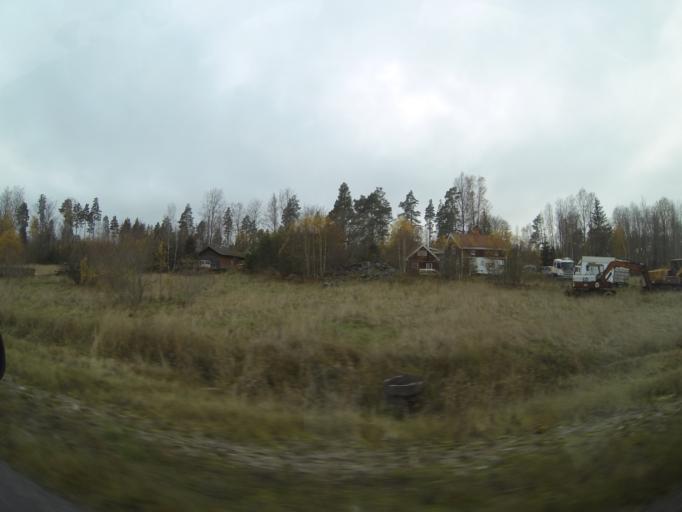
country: SE
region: Vaestmanland
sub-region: Surahammars Kommun
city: Ramnas
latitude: 59.7714
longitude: 16.1904
